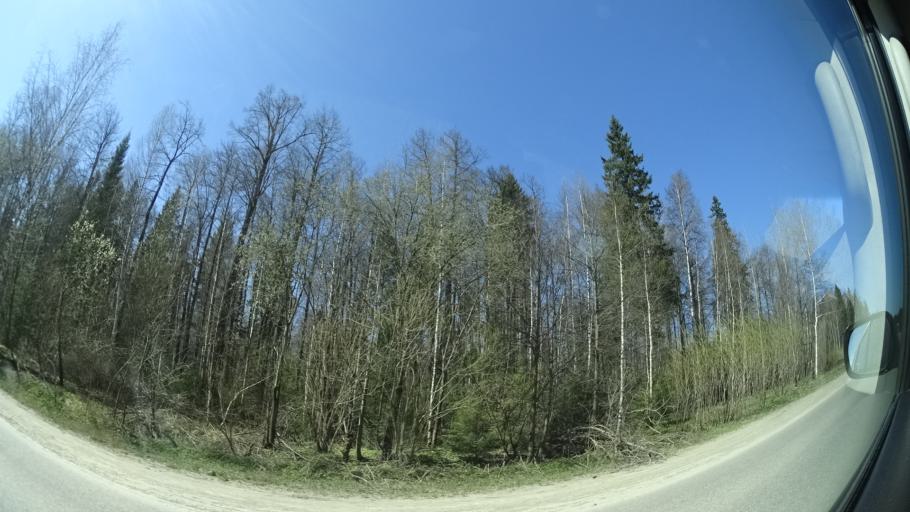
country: RU
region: Perm
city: Perm
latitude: 58.1338
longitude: 56.3024
